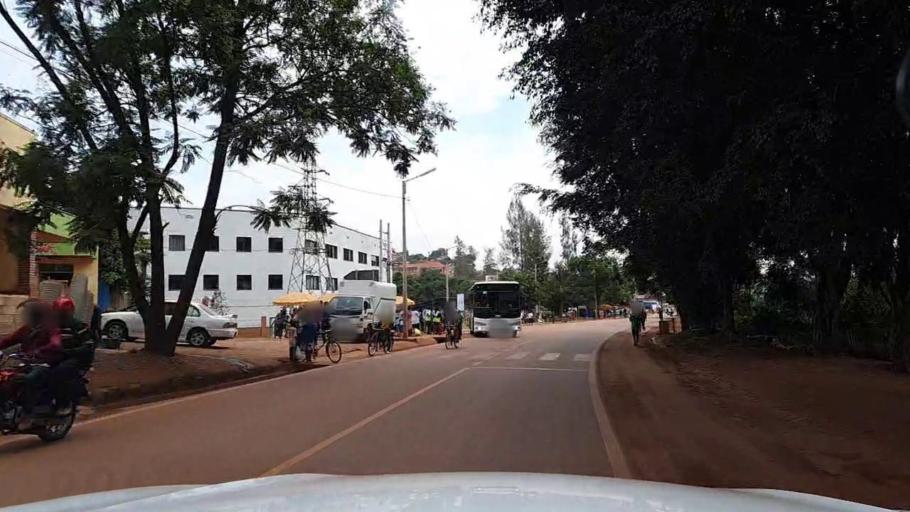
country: RW
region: Kigali
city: Kigali
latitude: -1.9042
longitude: 30.0503
